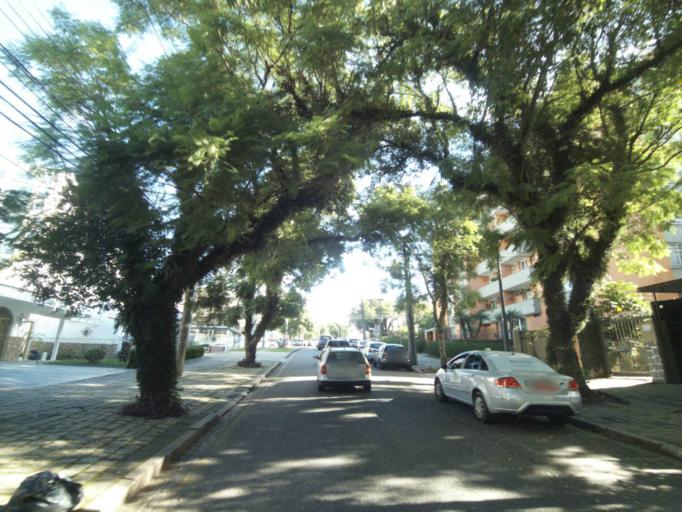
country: BR
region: Parana
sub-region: Curitiba
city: Curitiba
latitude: -25.4389
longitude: -49.2877
